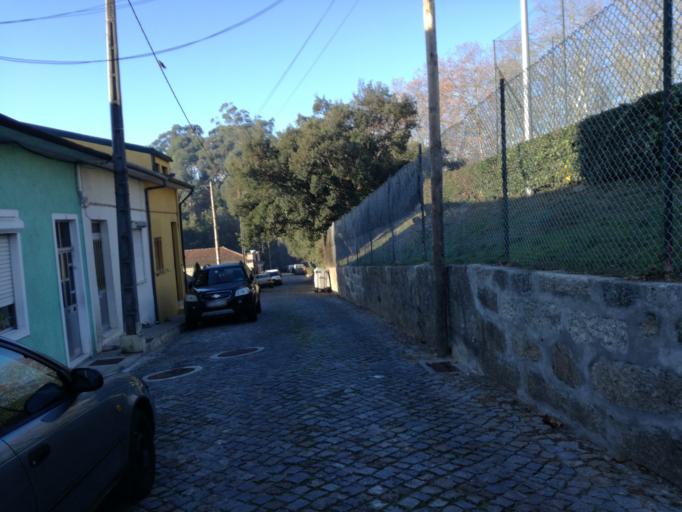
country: PT
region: Porto
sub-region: Maia
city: Leca do Bailio
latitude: 41.2110
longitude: -8.6141
